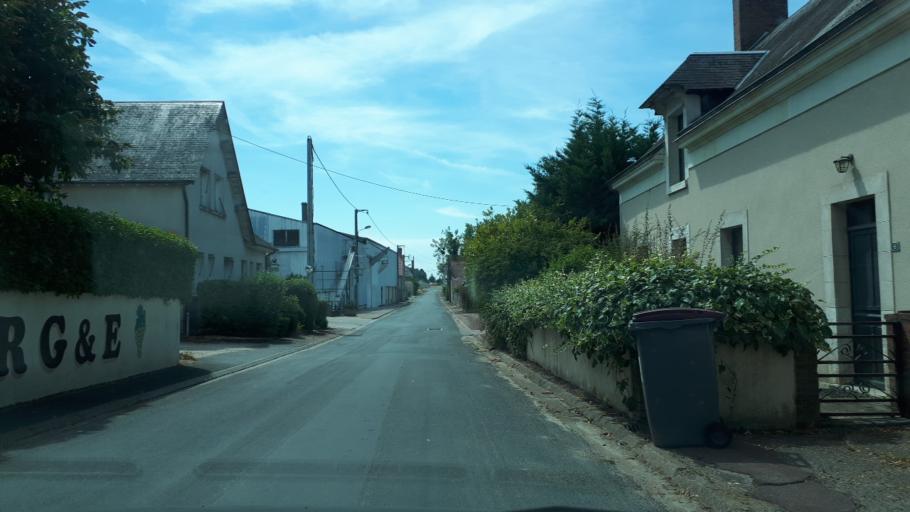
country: FR
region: Centre
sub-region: Departement du Loir-et-Cher
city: Contres
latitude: 47.3897
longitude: 1.3778
